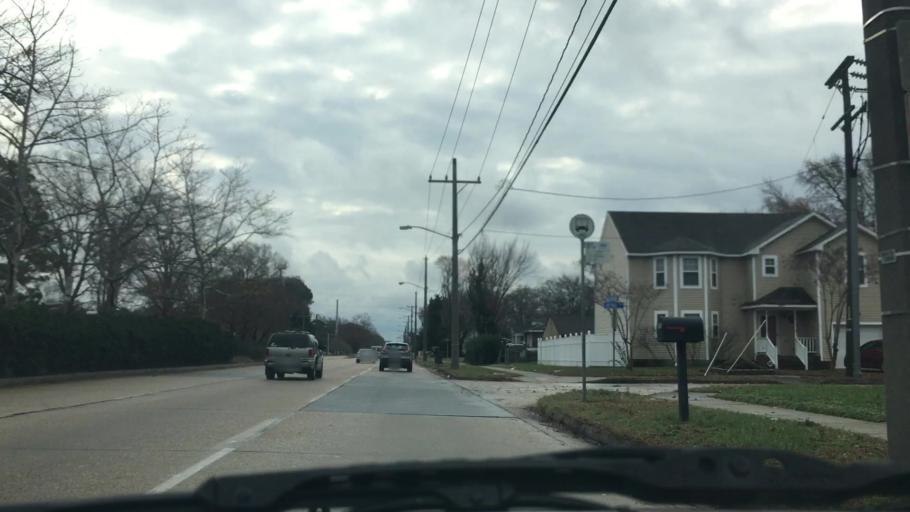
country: US
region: Virginia
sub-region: City of Norfolk
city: Norfolk
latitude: 36.9128
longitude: -76.2413
